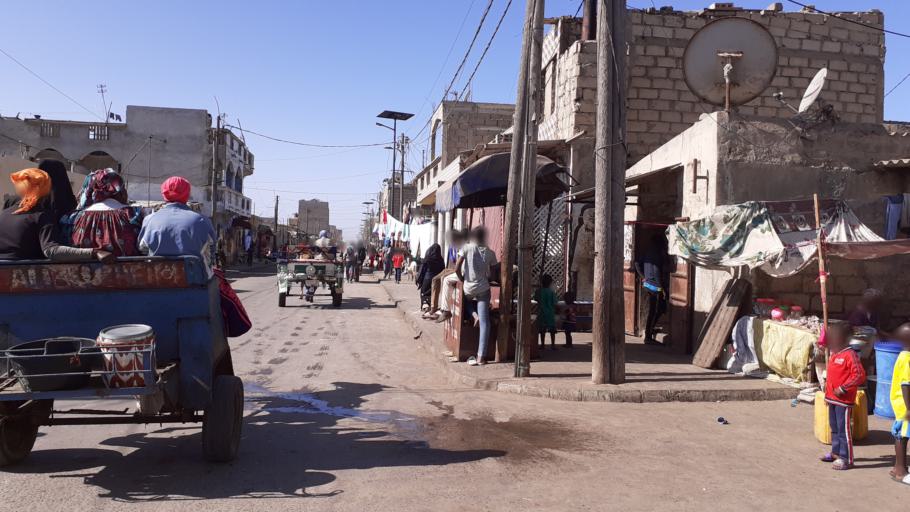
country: SN
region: Saint-Louis
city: Saint-Louis
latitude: 16.0223
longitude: -16.5088
